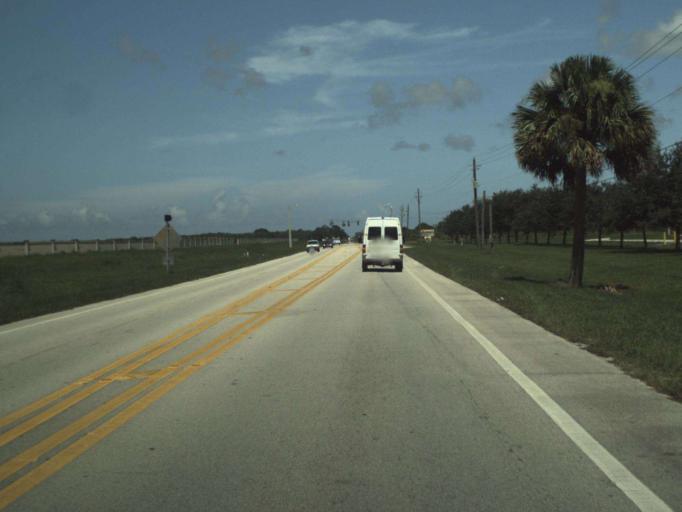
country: US
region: Florida
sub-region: Indian River County
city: Sebastian
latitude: 27.7488
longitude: -80.5098
